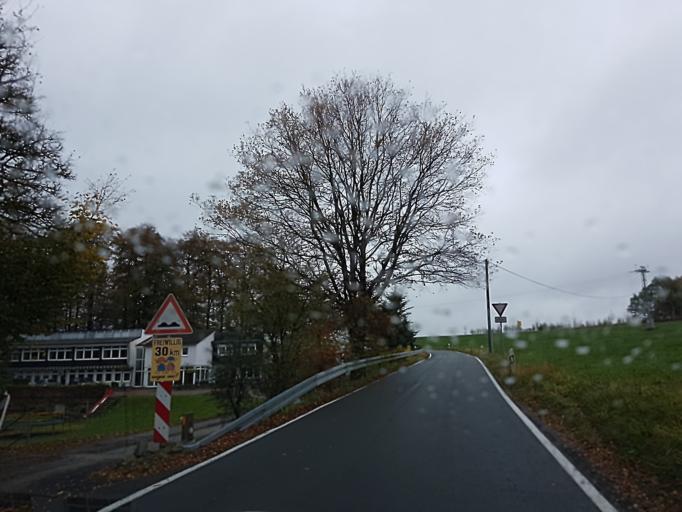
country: DE
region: North Rhine-Westphalia
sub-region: Regierungsbezirk Koln
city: Marienheide
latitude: 51.0921
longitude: 7.5733
